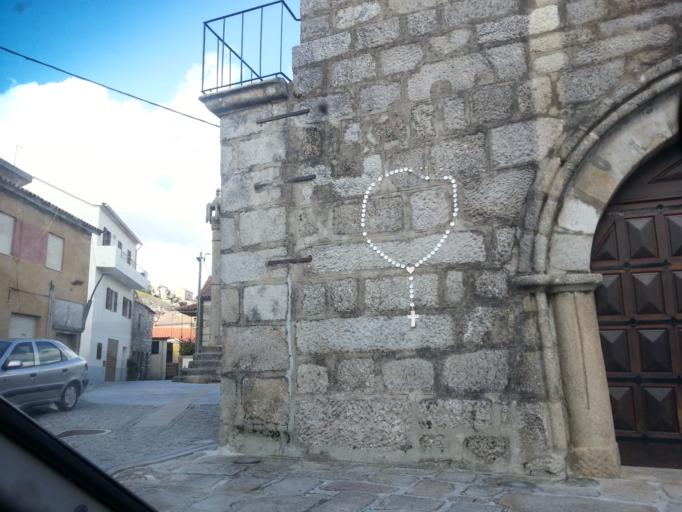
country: PT
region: Guarda
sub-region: Fornos de Algodres
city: Fornos de Algodres
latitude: 40.6453
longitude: -7.5166
